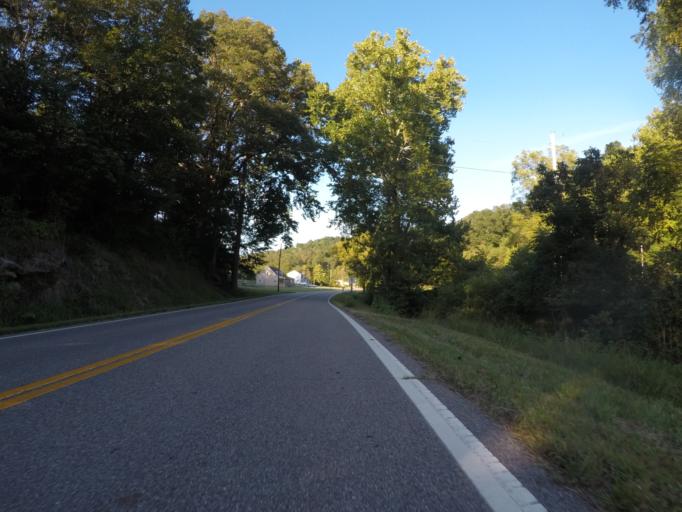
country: US
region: Ohio
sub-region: Lawrence County
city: Coal Grove
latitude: 38.5721
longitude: -82.5489
